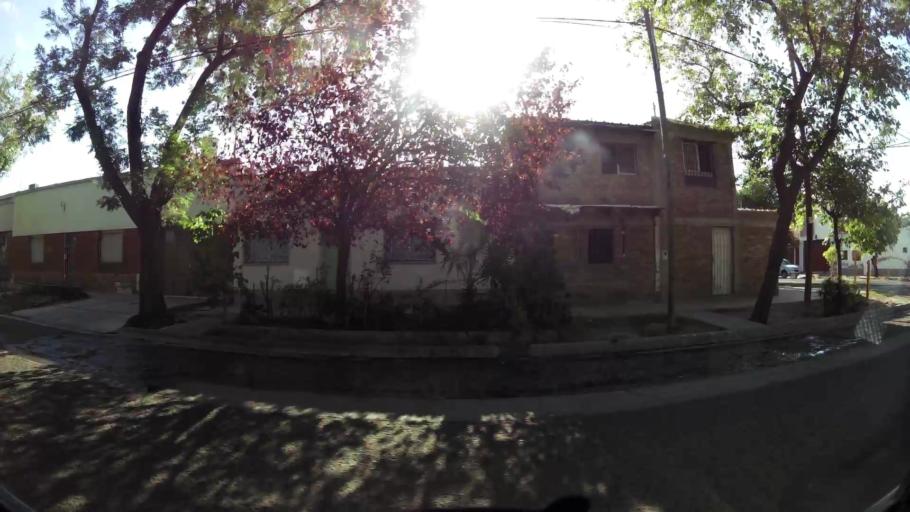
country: AR
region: Mendoza
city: Mendoza
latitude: -32.9024
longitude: -68.8211
